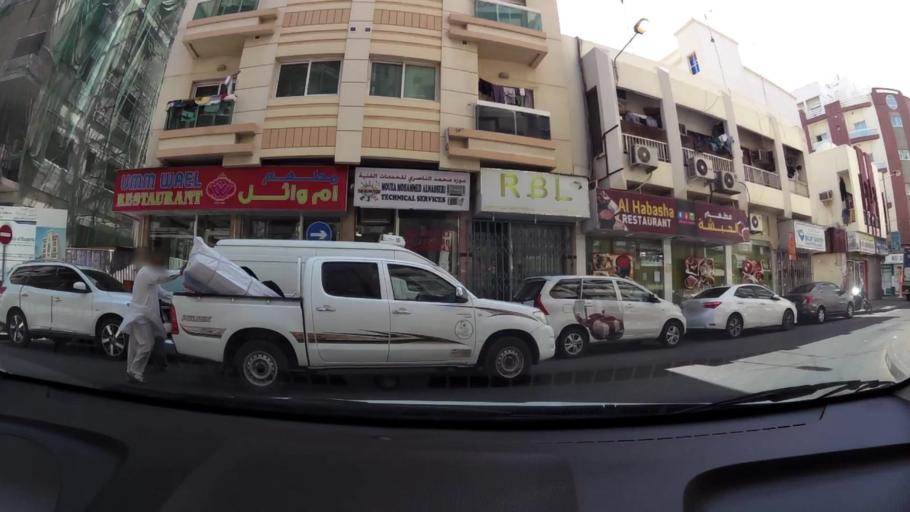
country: AE
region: Ash Shariqah
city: Sharjah
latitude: 25.2762
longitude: 55.3082
